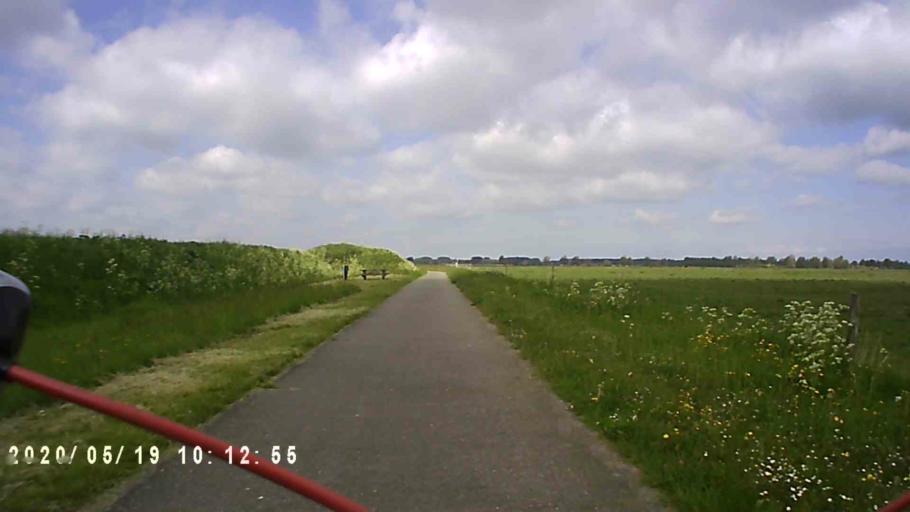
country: NL
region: Friesland
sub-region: Gemeente Kollumerland en Nieuwkruisland
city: Kollum
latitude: 53.3216
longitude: 6.2210
